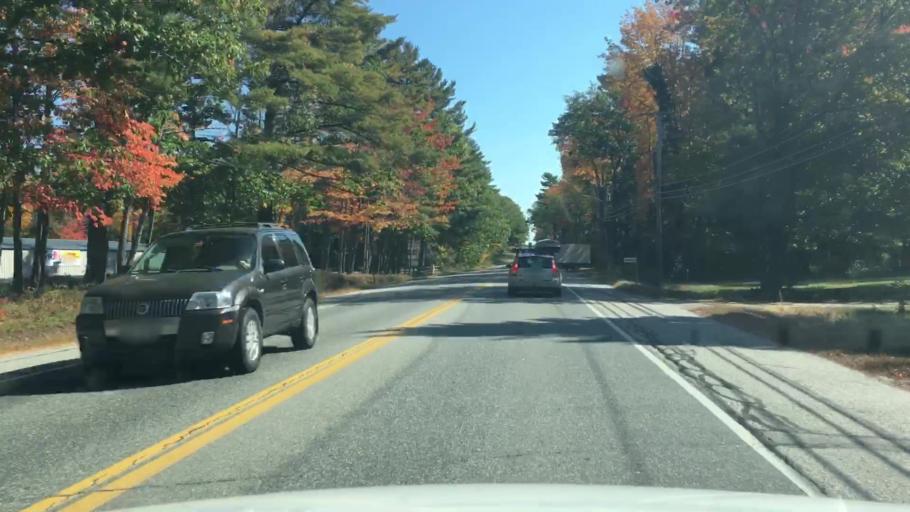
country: US
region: Maine
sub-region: Sagadahoc County
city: Topsham
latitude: 43.9515
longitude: -69.9944
